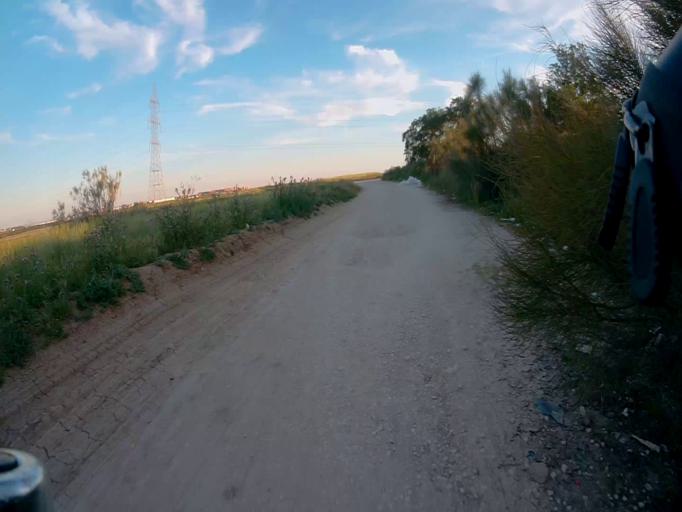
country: ES
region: Madrid
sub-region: Provincia de Madrid
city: Alcorcon
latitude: 40.3272
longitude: -3.8152
